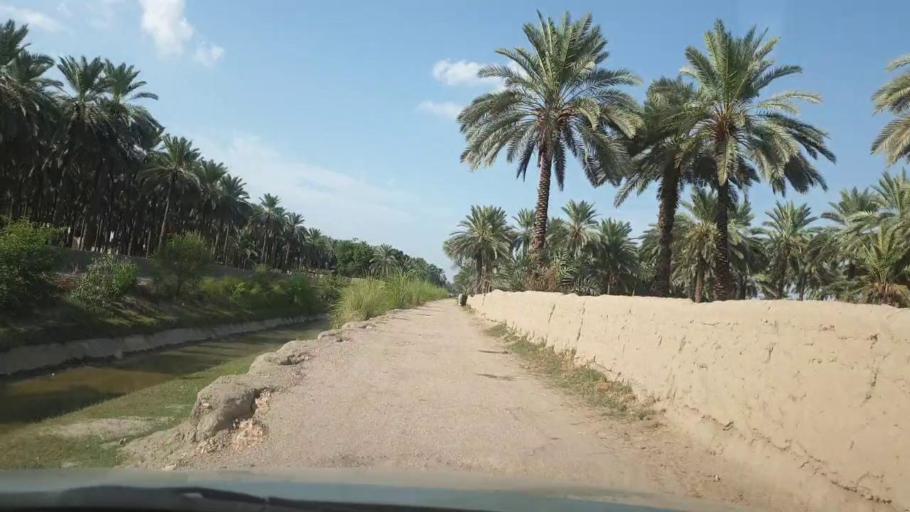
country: PK
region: Sindh
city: Sukkur
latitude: 27.6563
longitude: 68.8314
